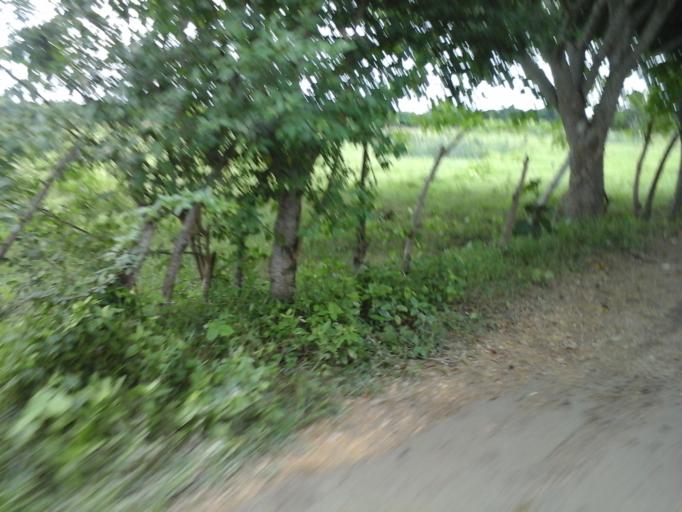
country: CO
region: Bolivar
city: San Pablo
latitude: 10.1518
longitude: -75.2738
